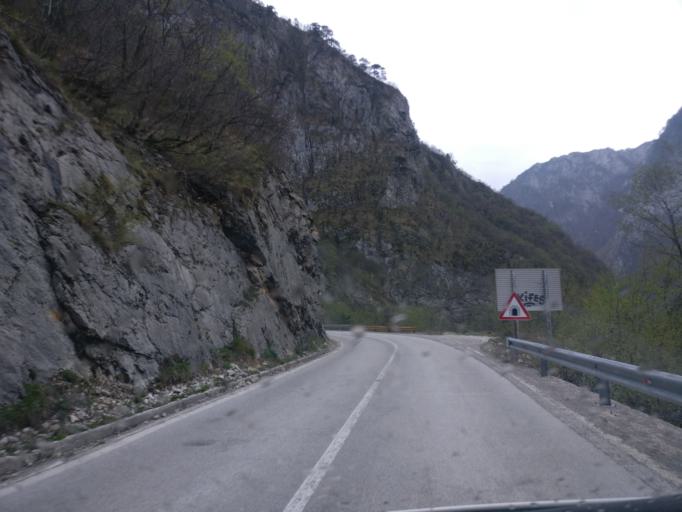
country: ME
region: Opstina Pluzine
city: Pluzine
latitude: 43.2292
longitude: 18.8467
